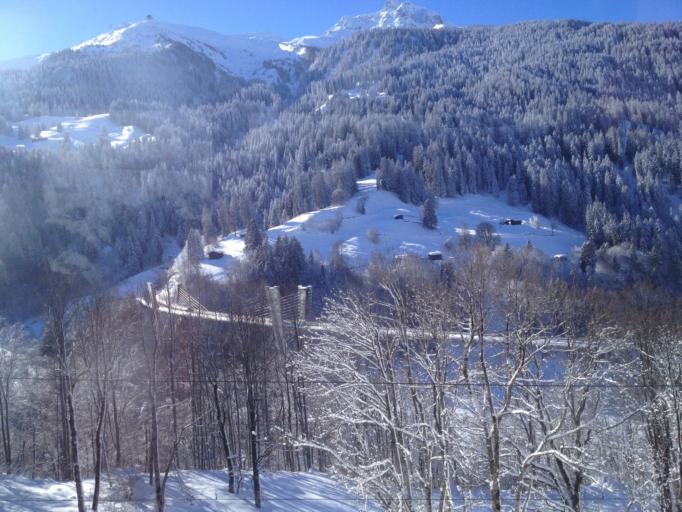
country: CH
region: Grisons
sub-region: Praettigau/Davos District
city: Klosters Serneus
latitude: 46.8867
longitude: 9.8584
